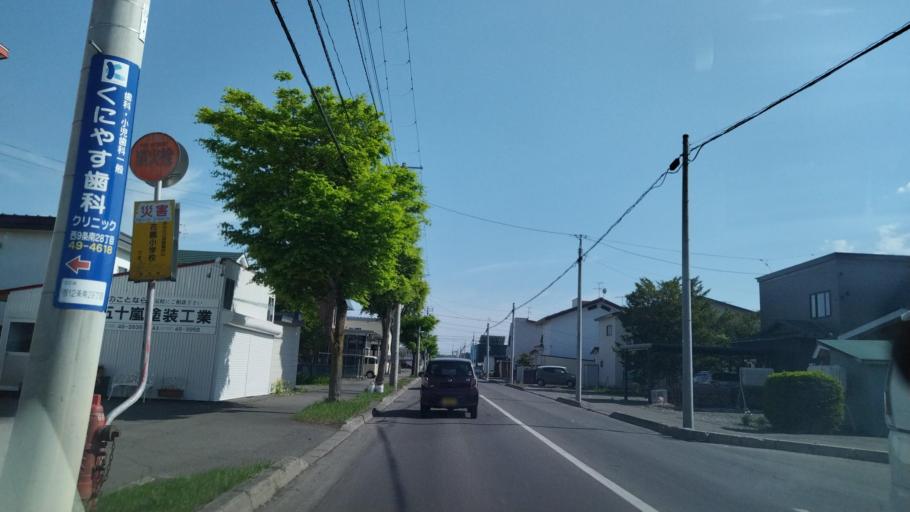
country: JP
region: Hokkaido
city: Obihiro
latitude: 42.8978
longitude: 143.1880
